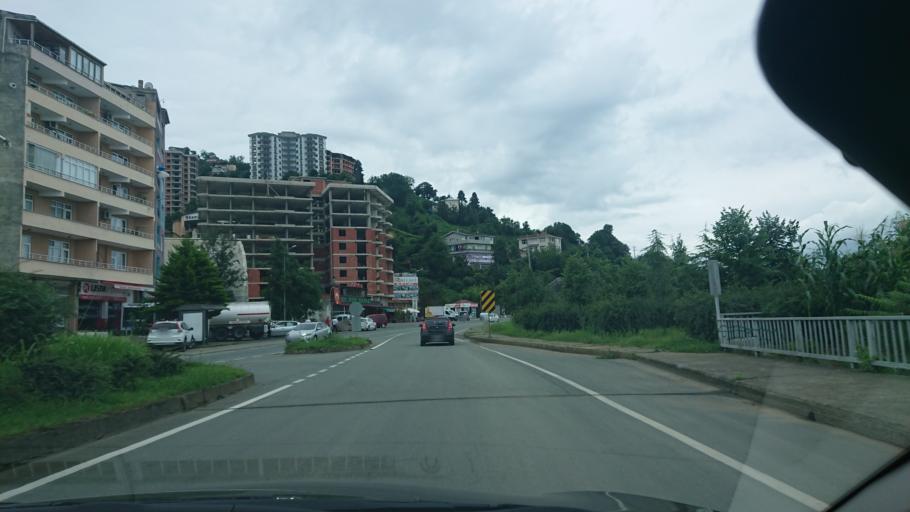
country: TR
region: Rize
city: Rize
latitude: 41.0346
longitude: 40.4790
